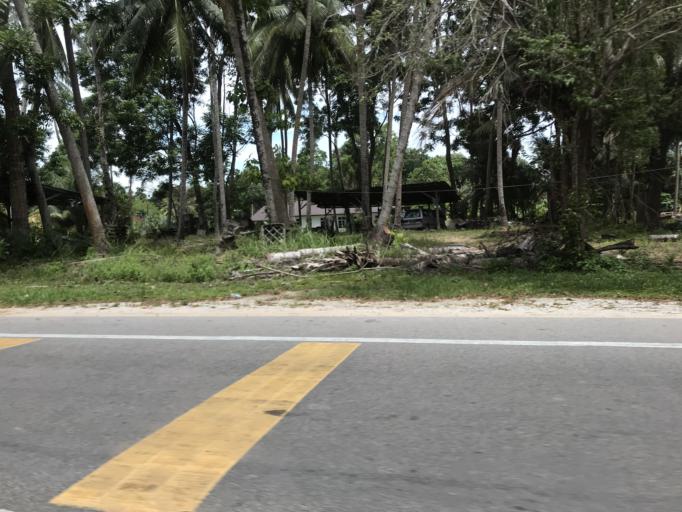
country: MY
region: Kelantan
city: Tumpat
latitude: 6.1705
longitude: 102.1893
